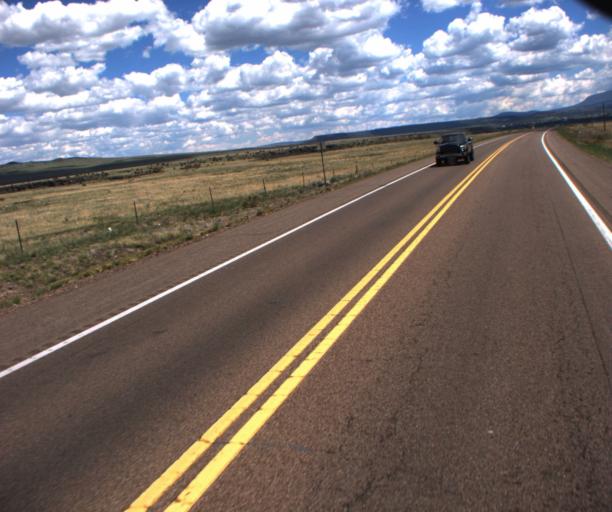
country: US
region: Arizona
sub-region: Apache County
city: Springerville
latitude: 34.1698
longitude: -109.3131
